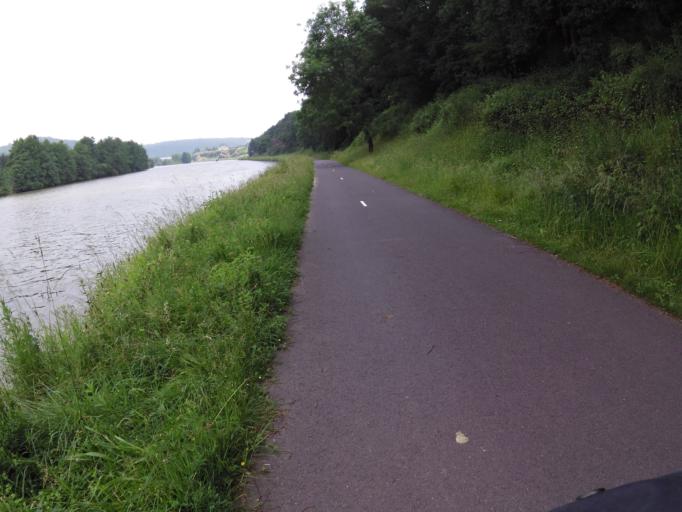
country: FR
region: Champagne-Ardenne
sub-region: Departement des Ardennes
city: Vireux-Molhain
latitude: 50.0737
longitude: 4.7284
